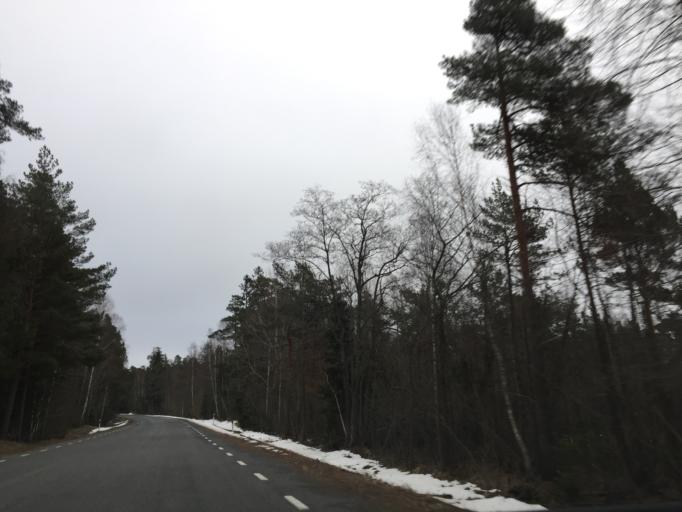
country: EE
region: Saare
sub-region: Kuressaare linn
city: Kuressaare
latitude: 58.4384
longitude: 22.2240
